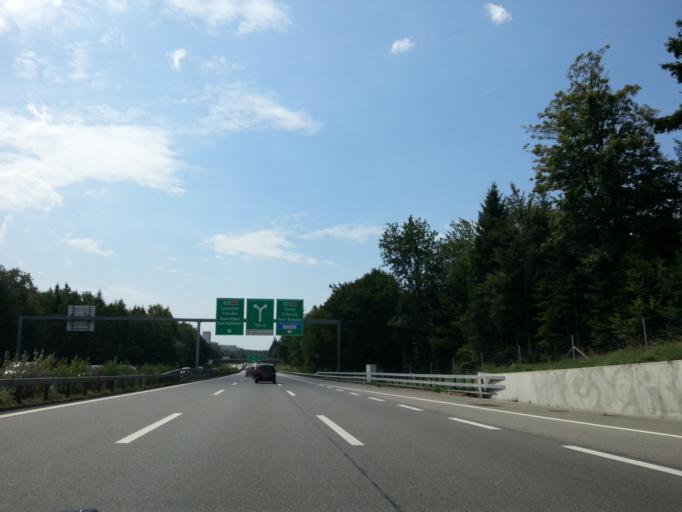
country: CH
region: Bern
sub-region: Bern-Mittelland District
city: Bern
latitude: 46.9619
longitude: 7.4252
